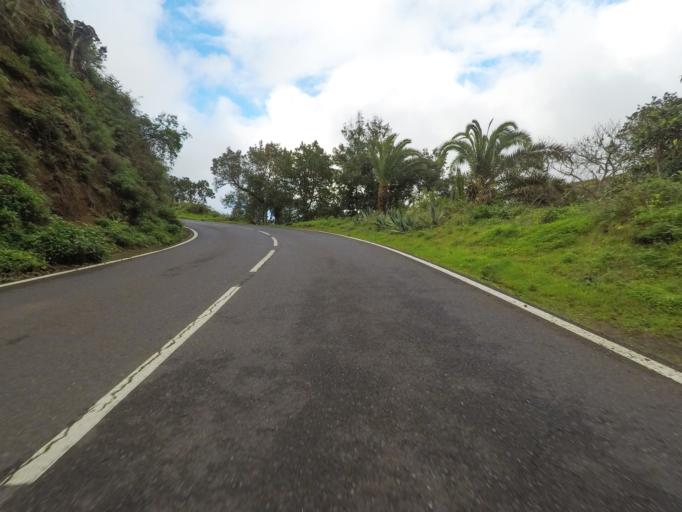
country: ES
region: Canary Islands
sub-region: Provincia de Santa Cruz de Tenerife
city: Hermigua
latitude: 28.1313
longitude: -17.2005
